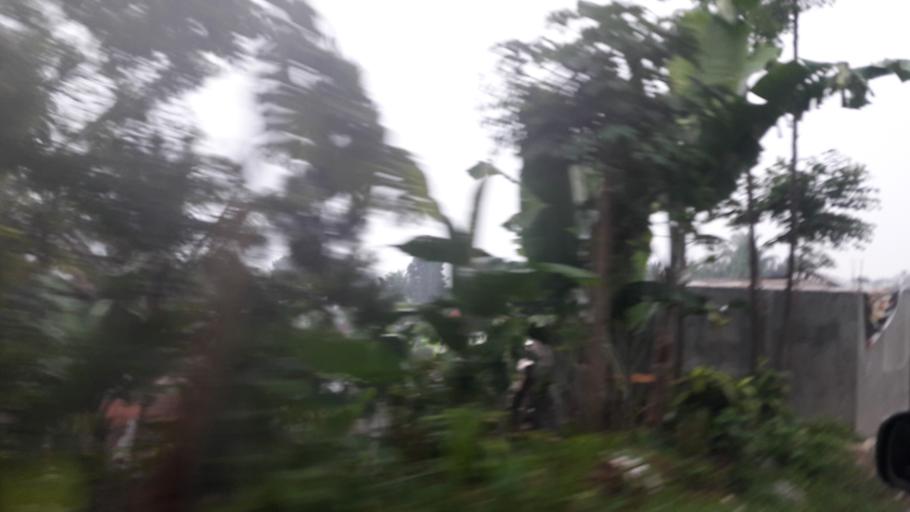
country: ID
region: West Java
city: Cipeundeuy
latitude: -6.6474
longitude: 106.5207
